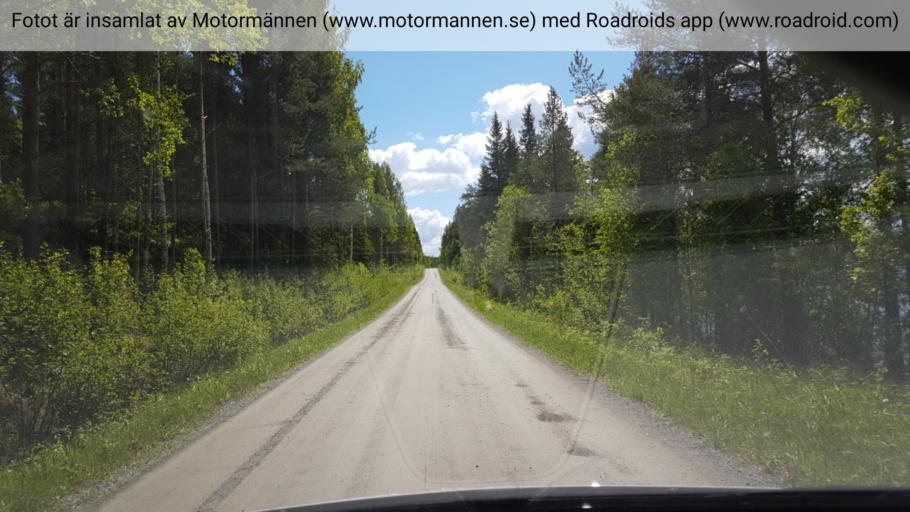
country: SE
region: Jaemtland
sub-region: OEstersunds Kommun
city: Brunflo
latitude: 63.0239
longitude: 15.0914
